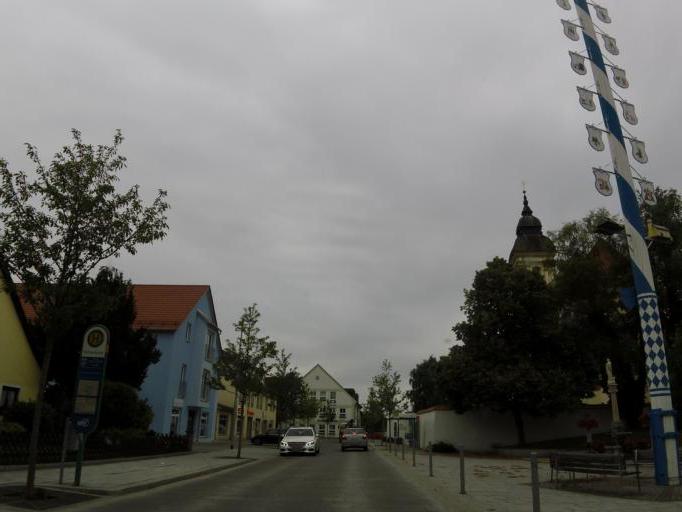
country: DE
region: Bavaria
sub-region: Upper Bavaria
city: Erding
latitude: 48.2933
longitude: 11.9065
